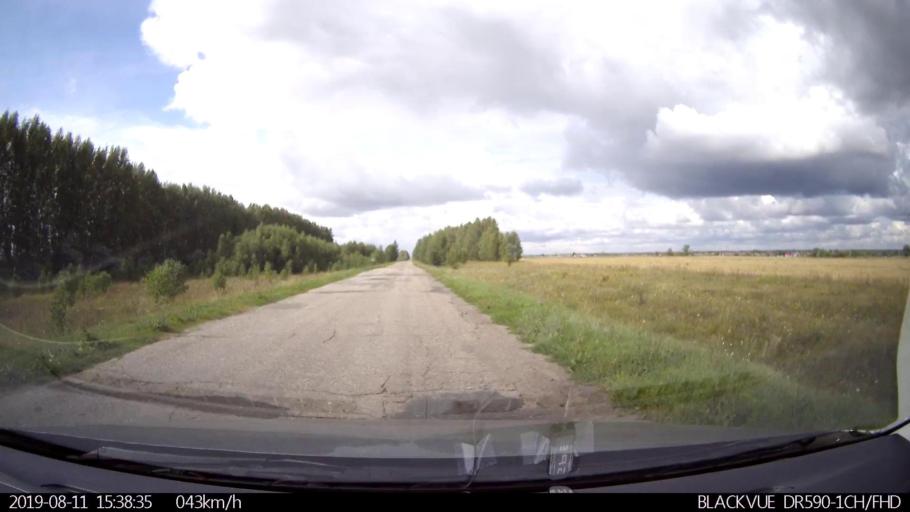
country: RU
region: Ulyanovsk
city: Ignatovka
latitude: 53.8623
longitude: 47.6405
